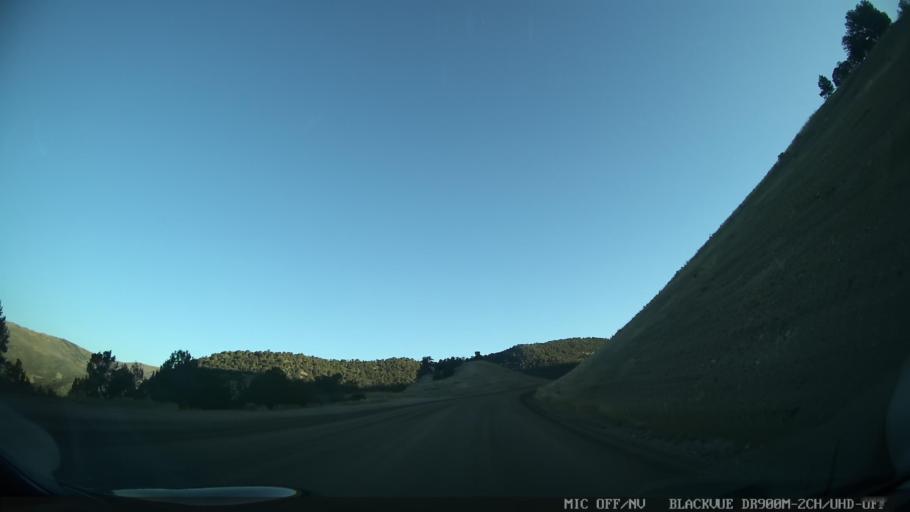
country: US
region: Colorado
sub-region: Grand County
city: Kremmling
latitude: 39.9451
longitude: -106.5290
